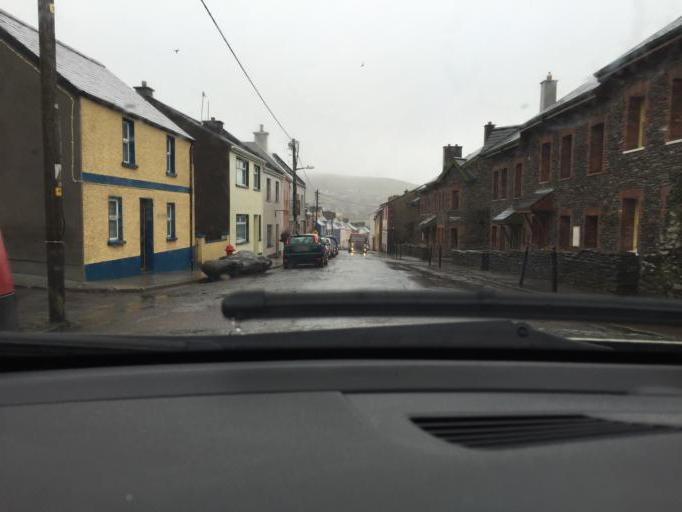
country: IE
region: Munster
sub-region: Ciarrai
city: Dingle
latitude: 52.1433
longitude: -10.2720
